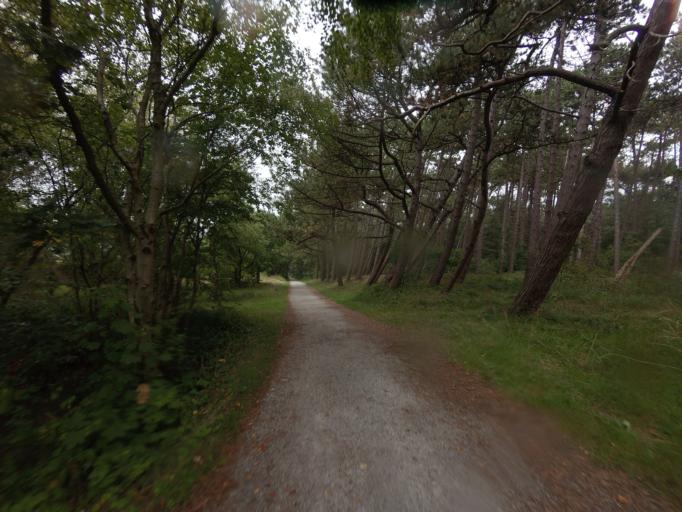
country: NL
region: Friesland
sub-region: Gemeente Schiermonnikoog
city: Schiermonnikoog
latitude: 53.4839
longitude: 6.1637
